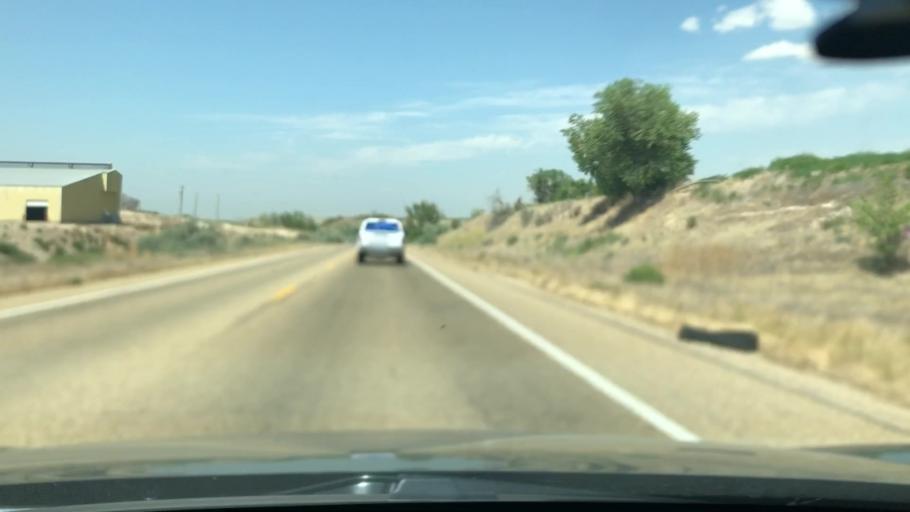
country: US
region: Idaho
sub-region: Canyon County
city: Wilder
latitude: 43.7129
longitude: -116.9118
